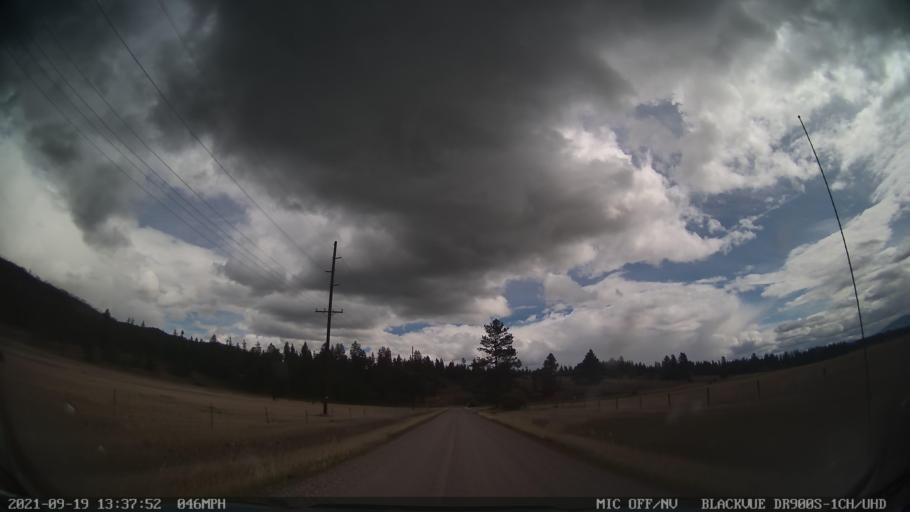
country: US
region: Montana
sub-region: Missoula County
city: Seeley Lake
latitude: 47.1066
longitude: -113.2762
